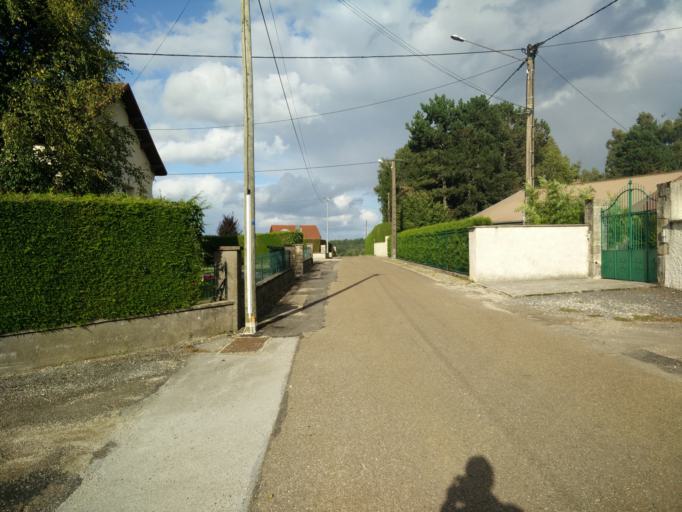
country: FR
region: Franche-Comte
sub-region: Departement du Doubs
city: Saone
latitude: 47.2277
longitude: 6.1257
